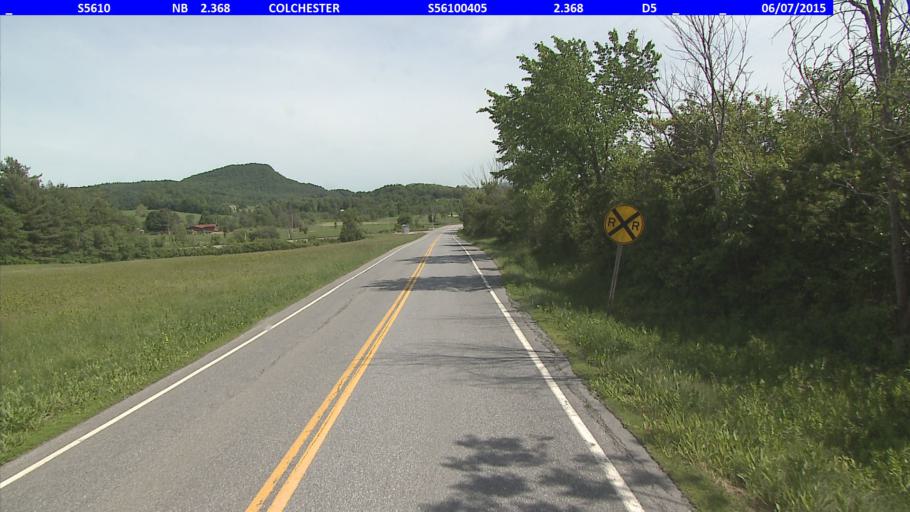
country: US
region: Vermont
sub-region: Chittenden County
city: Colchester
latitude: 44.5736
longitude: -73.1273
